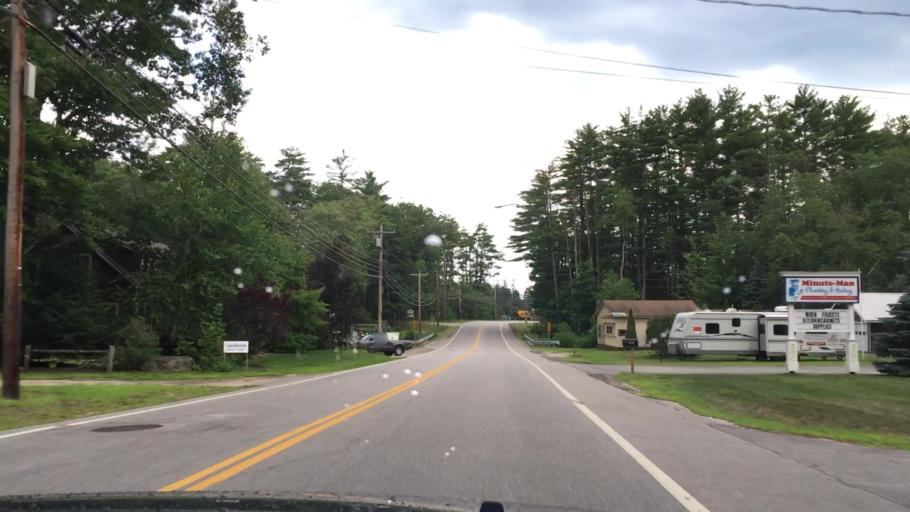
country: US
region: New Hampshire
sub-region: Belknap County
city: Meredith
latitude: 43.6724
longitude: -71.5044
